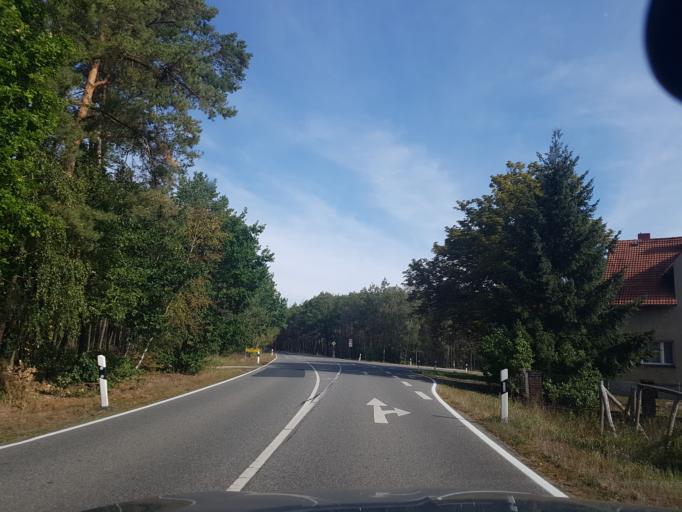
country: DE
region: Brandenburg
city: Schilda
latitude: 51.6420
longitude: 13.3708
